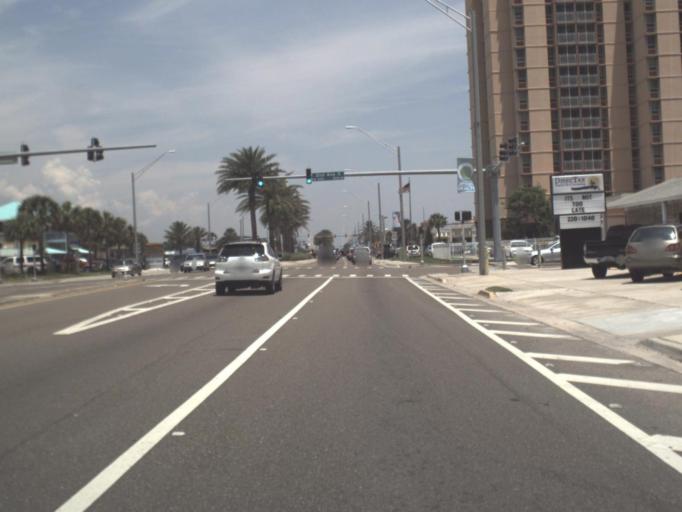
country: US
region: Florida
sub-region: Duval County
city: Jacksonville Beach
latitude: 30.2857
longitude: -81.3912
